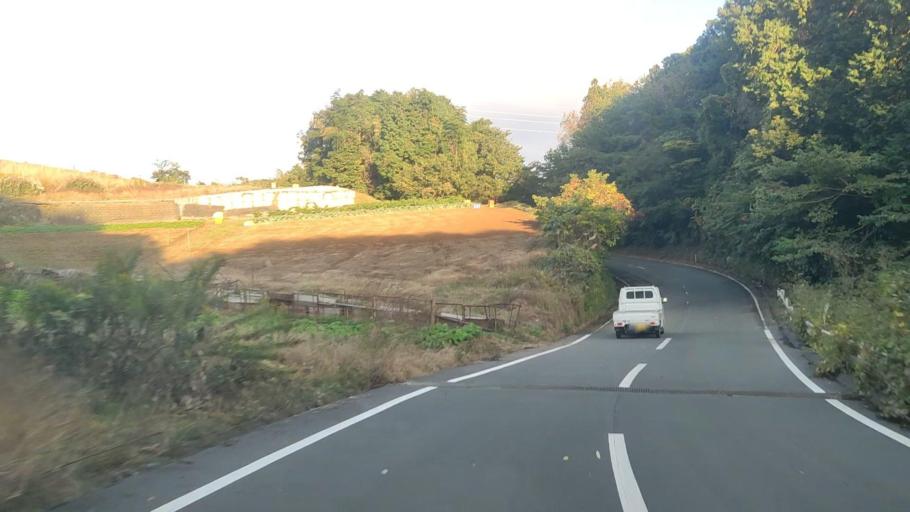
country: JP
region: Shizuoka
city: Mishima
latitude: 35.1315
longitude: 138.9784
